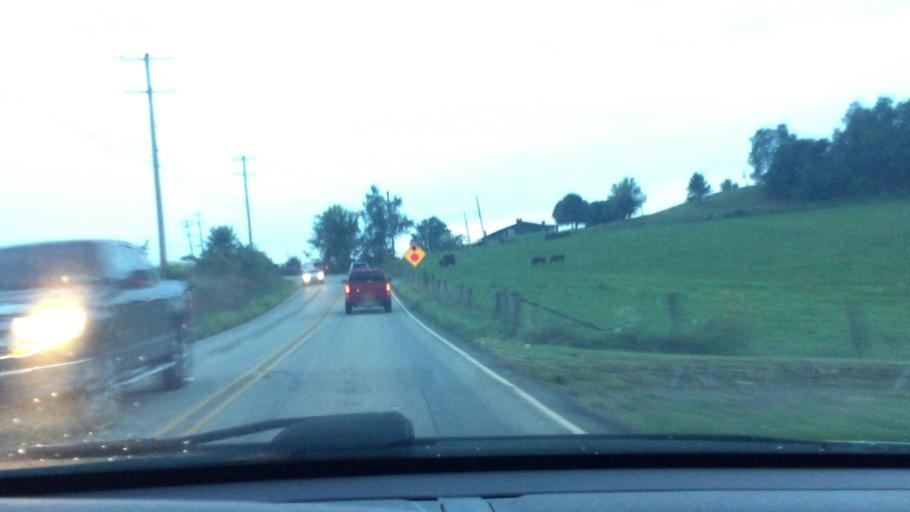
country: US
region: Pennsylvania
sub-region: Washington County
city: McGovern
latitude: 40.1984
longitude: -80.1961
